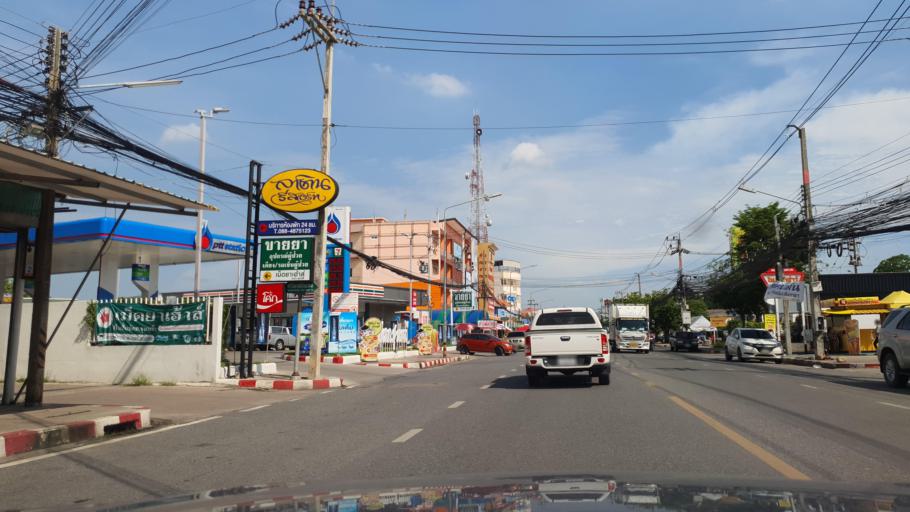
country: TH
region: Chachoengsao
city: Chachoengsao
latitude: 13.6829
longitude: 101.0667
